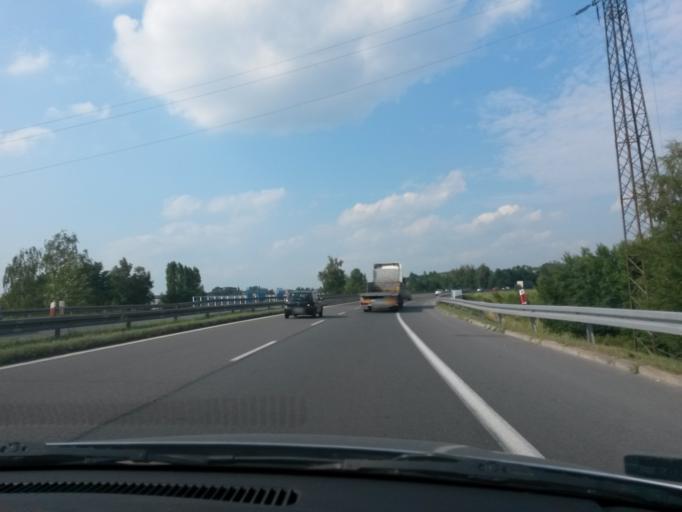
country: PL
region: Silesian Voivodeship
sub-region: Myslowice
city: Myslowice
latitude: 50.2649
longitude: 19.1913
